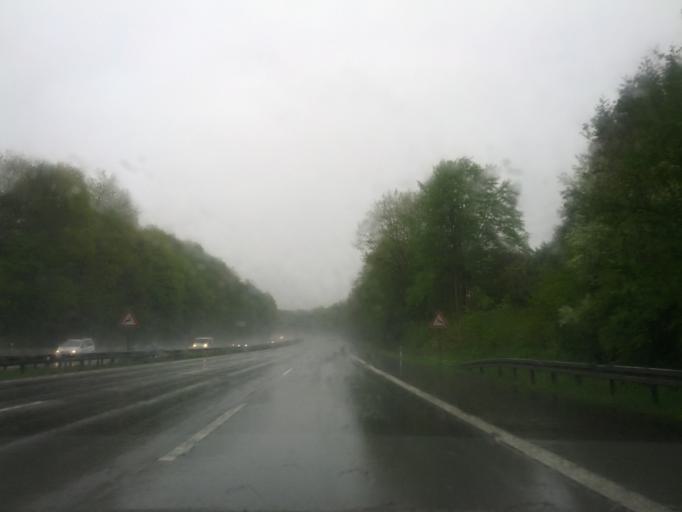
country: DE
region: North Rhine-Westphalia
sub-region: Regierungsbezirk Koln
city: Overath
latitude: 50.9470
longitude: 7.2212
